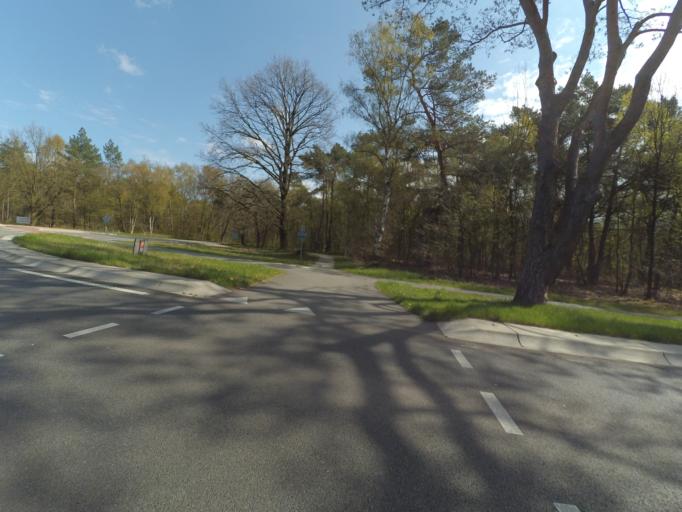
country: NL
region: Gelderland
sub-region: Gemeente Oldebroek
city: Oldebroek
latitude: 52.3810
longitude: 5.9133
